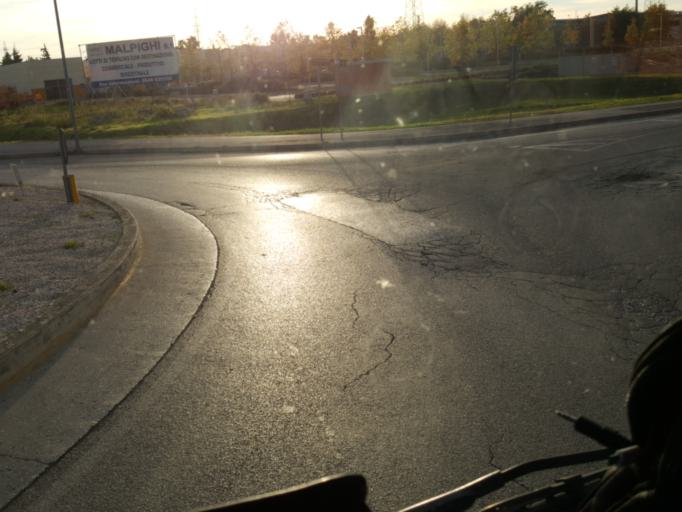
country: IT
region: Emilia-Romagna
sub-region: Provincia di Ravenna
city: Faenza
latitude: 44.3013
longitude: 11.8697
